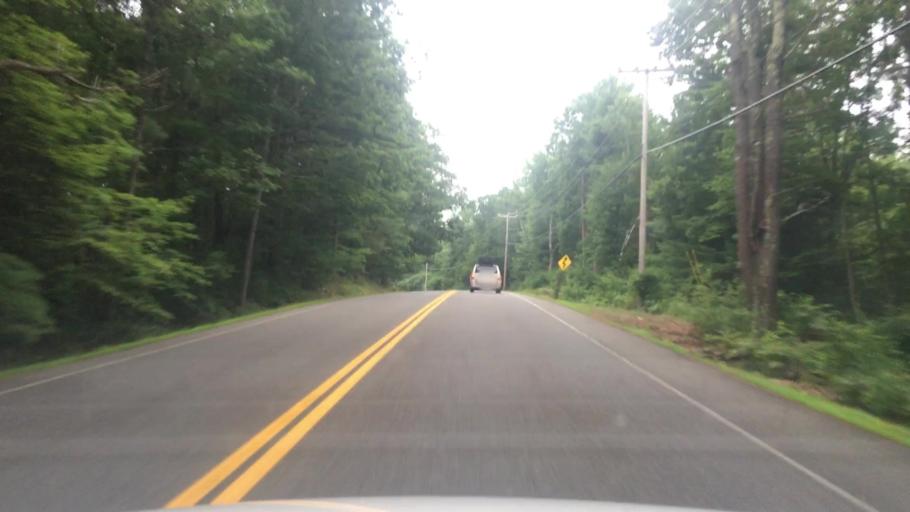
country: US
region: Maine
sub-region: York County
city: Wells Beach Station
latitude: 43.3154
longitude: -70.5980
